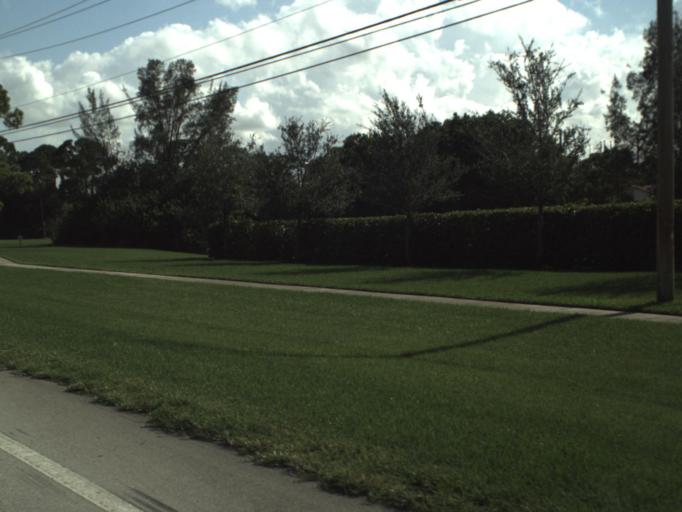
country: US
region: Florida
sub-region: Palm Beach County
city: Villages of Oriole
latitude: 26.4103
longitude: -80.2041
